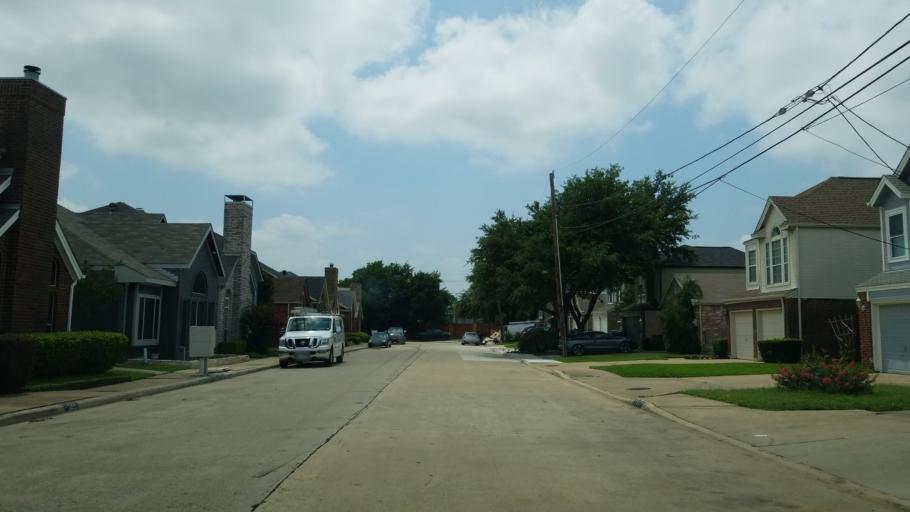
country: US
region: Texas
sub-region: Dallas County
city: Farmers Branch
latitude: 32.9079
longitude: -96.8795
